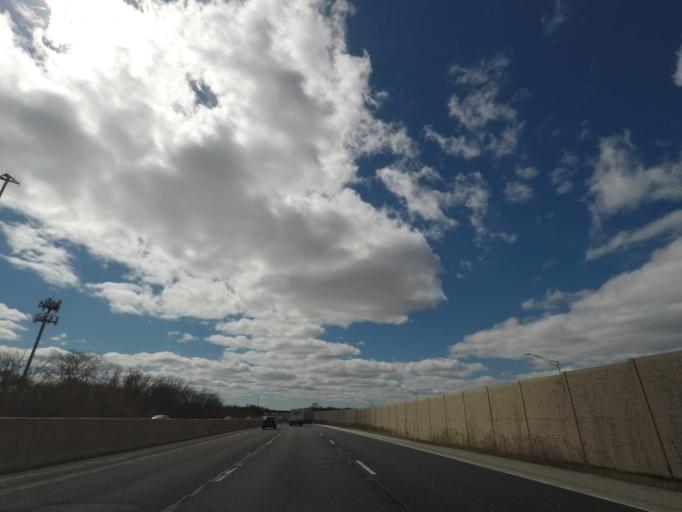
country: US
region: Illinois
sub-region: Will County
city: Crystal Lawns
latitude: 41.5692
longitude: -88.1811
